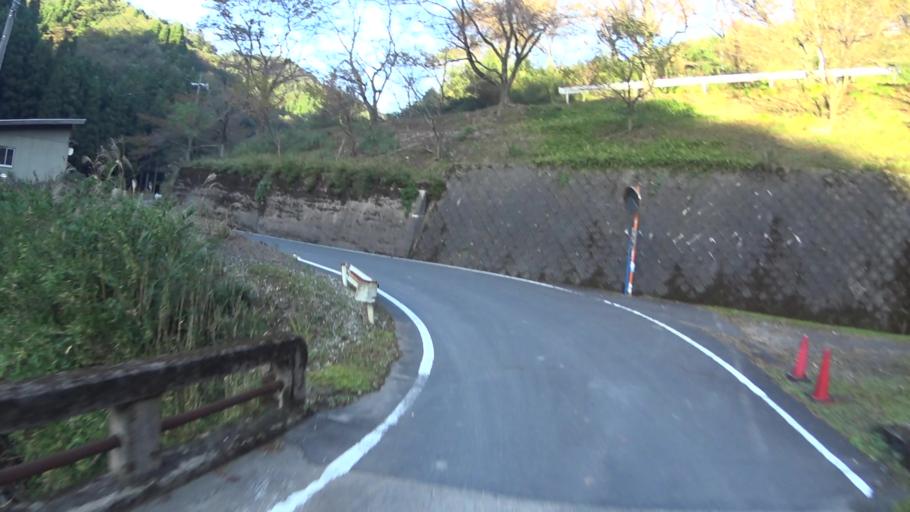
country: JP
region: Hyogo
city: Toyooka
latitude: 35.6242
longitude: 134.9788
